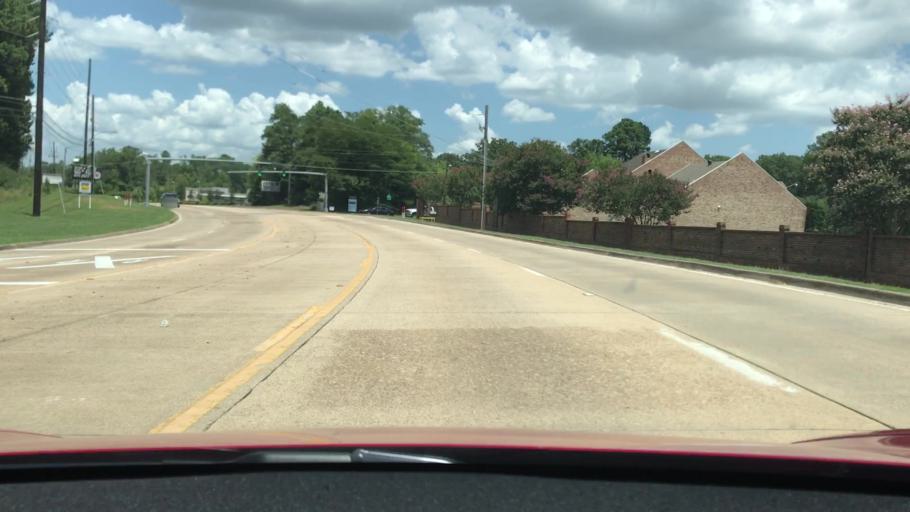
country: US
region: Louisiana
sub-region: Bossier Parish
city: Bossier City
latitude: 32.4206
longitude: -93.7360
